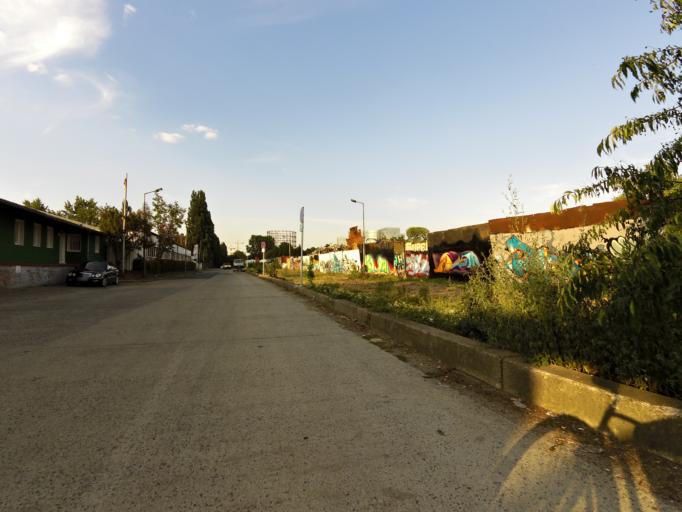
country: DE
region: Berlin
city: Berlin Schoeneberg
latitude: 52.4764
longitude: 13.3499
